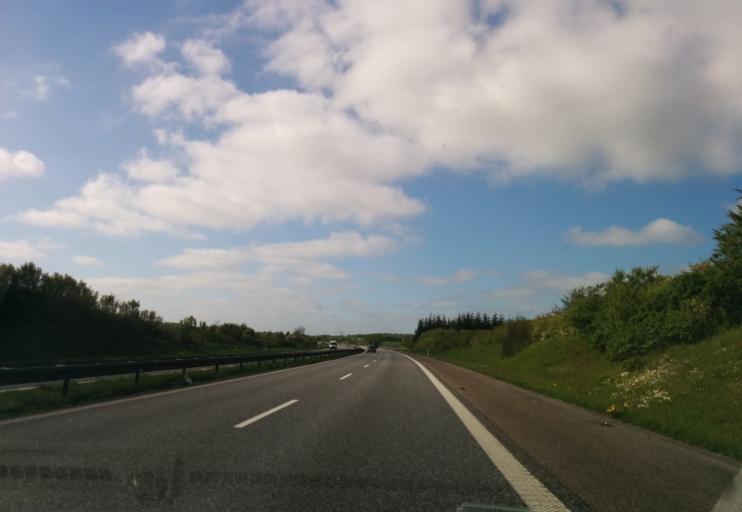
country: DK
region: South Denmark
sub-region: Fredericia Kommune
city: Taulov
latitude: 55.5854
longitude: 9.6089
